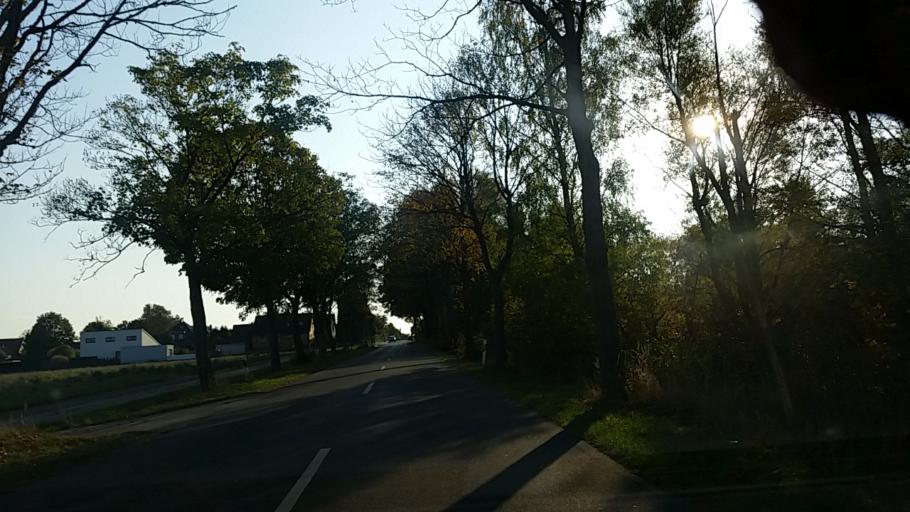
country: DE
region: Lower Saxony
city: Wolfsburg
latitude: 52.3539
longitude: 10.7800
